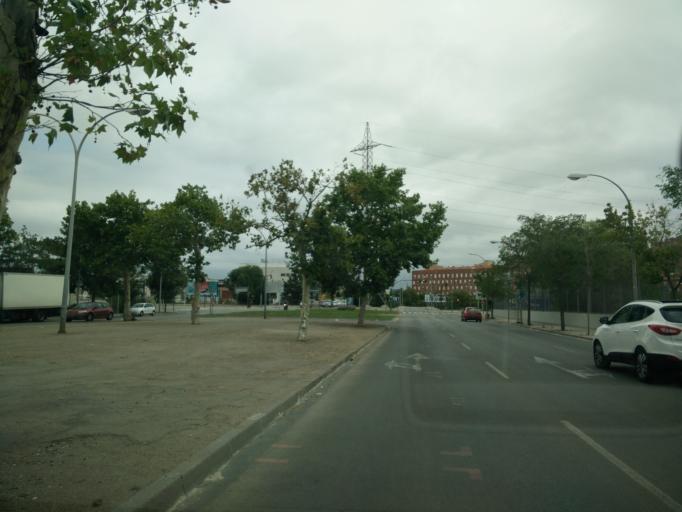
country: ES
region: Catalonia
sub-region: Provincia de Barcelona
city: Terrassa
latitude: 41.5803
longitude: 2.0255
